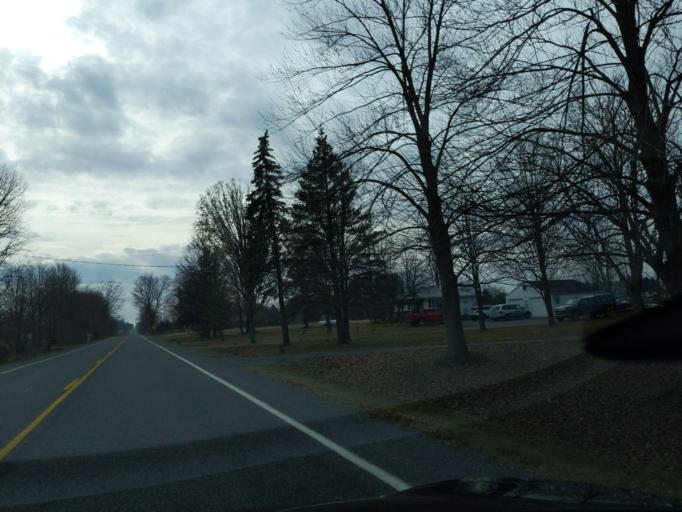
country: US
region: Michigan
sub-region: Ingham County
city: Mason
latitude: 42.5420
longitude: -84.5225
